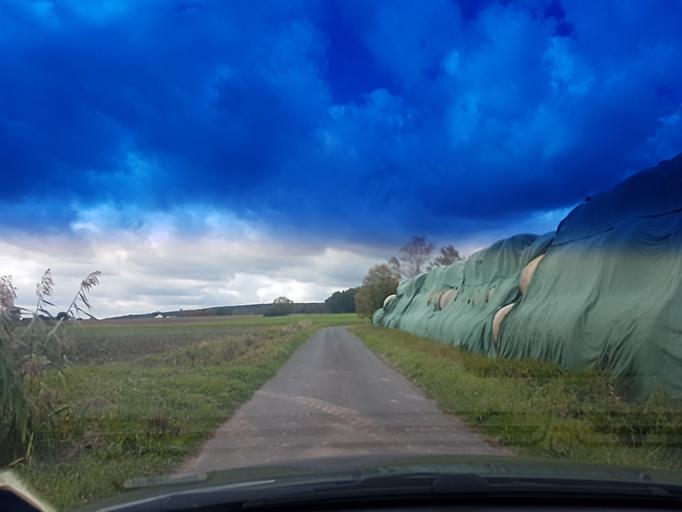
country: DE
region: Bavaria
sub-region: Regierungsbezirk Mittelfranken
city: Wachenroth
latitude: 49.7504
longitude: 10.6816
